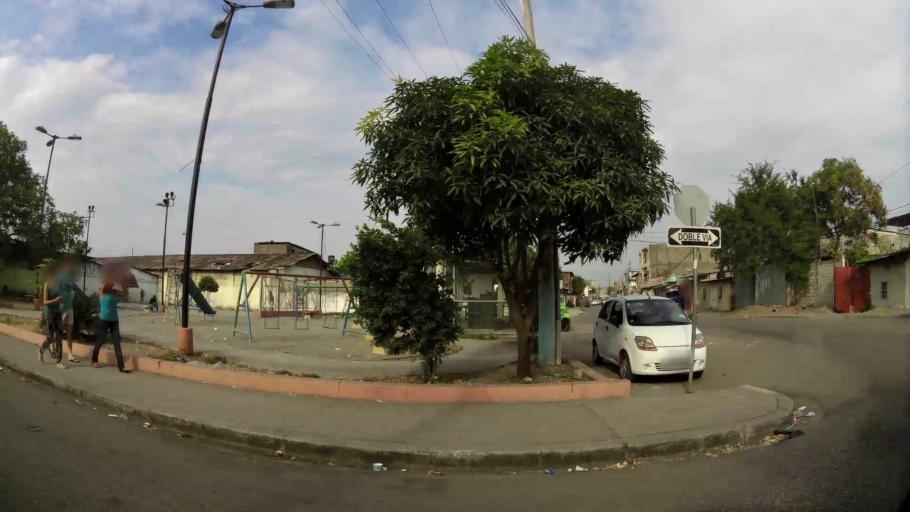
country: EC
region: Guayas
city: Guayaquil
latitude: -2.2498
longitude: -79.9073
